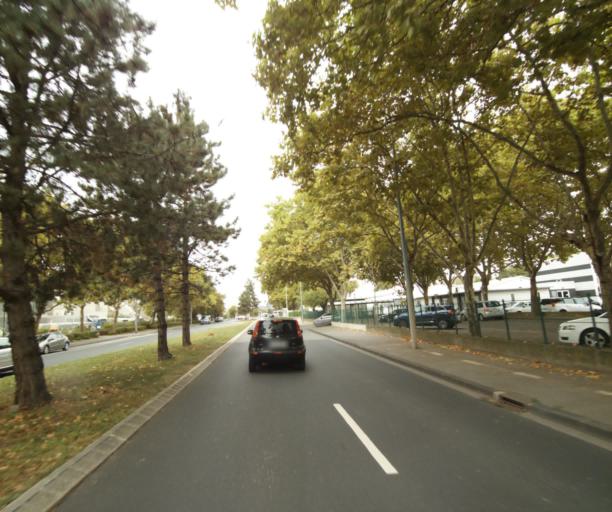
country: FR
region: Auvergne
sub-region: Departement du Puy-de-Dome
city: Gerzat
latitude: 45.7983
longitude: 3.1225
